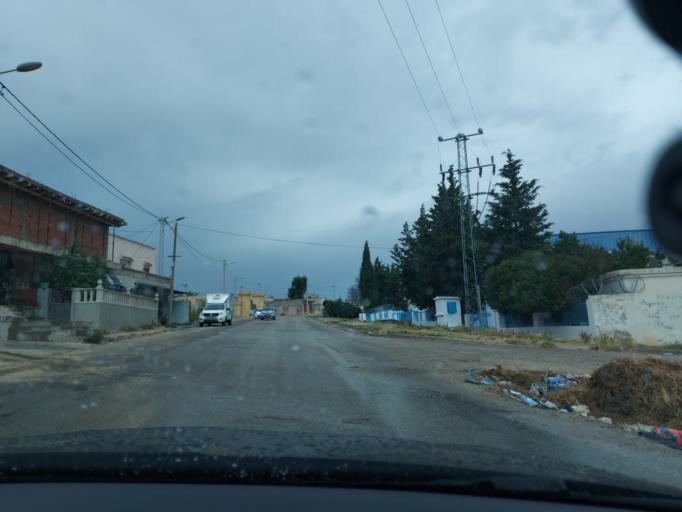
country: TN
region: Silyanah
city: Maktar
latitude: 35.8534
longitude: 9.2130
